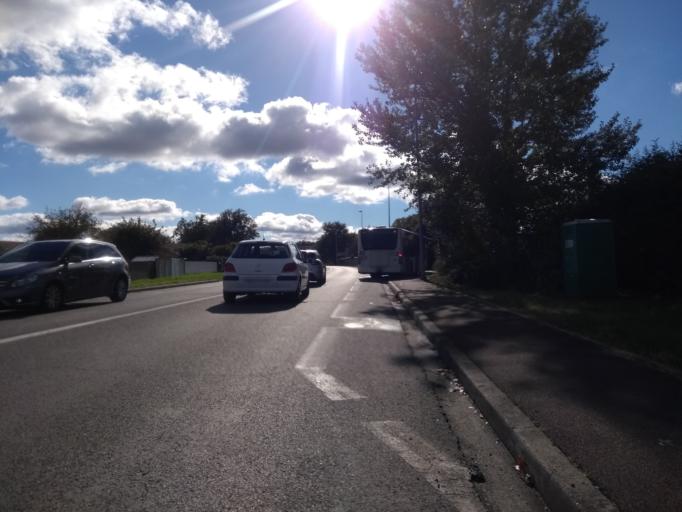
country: FR
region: Aquitaine
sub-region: Departement de la Gironde
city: Pessac
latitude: 44.8217
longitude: -0.6657
